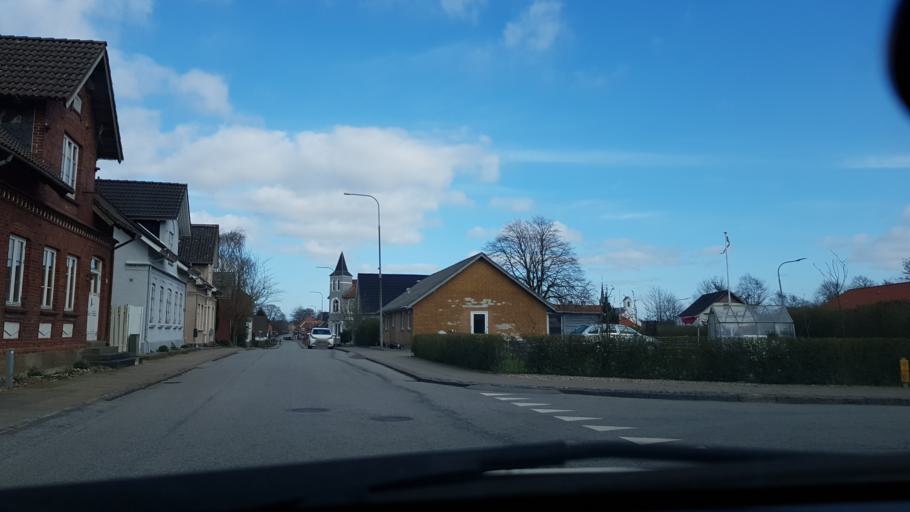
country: DK
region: South Denmark
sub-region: Vejen Kommune
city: Vejen
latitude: 55.4205
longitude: 9.1476
